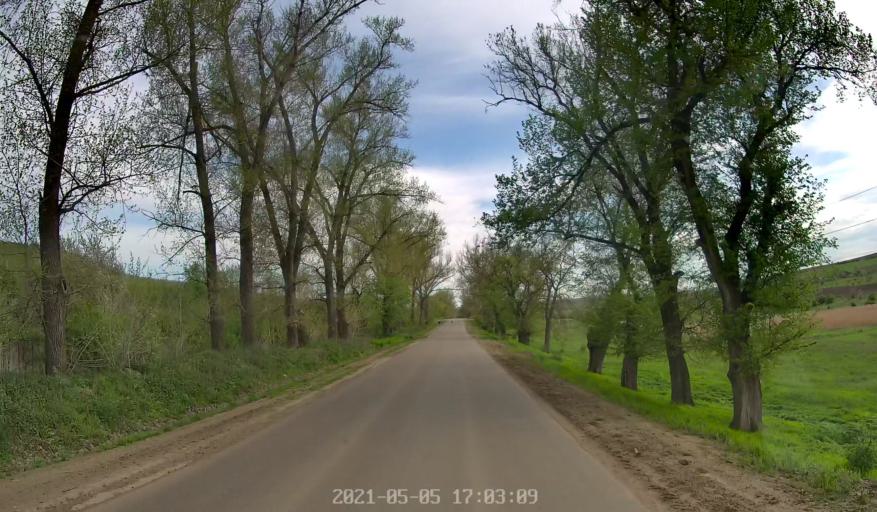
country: MD
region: Chisinau
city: Vadul lui Voda
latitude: 47.0537
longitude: 29.1329
